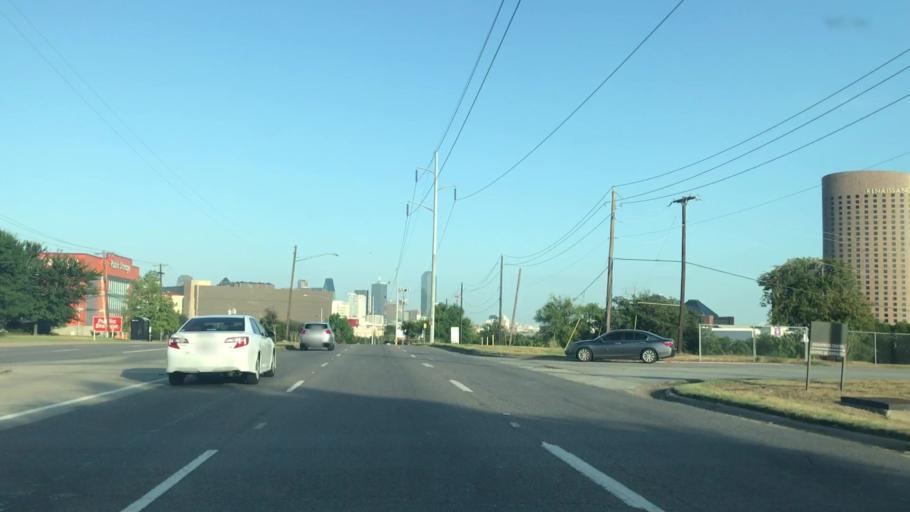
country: US
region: Texas
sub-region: Dallas County
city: Dallas
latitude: 32.8087
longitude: -96.8334
